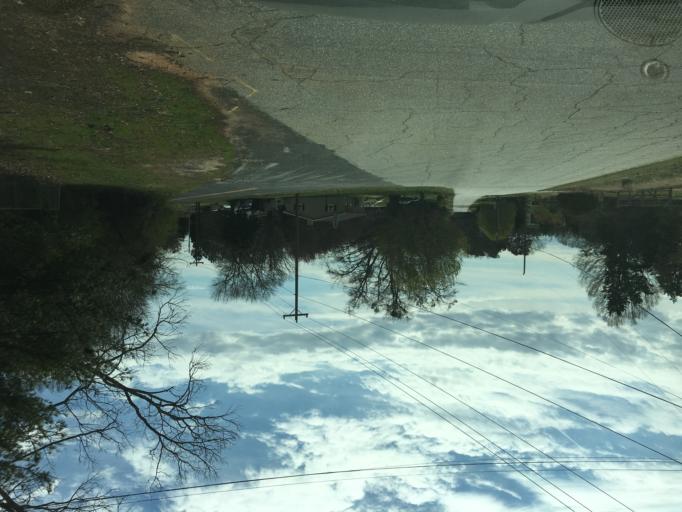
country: US
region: South Carolina
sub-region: Greenville County
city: Fountain Inn
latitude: 34.7021
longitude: -82.2262
